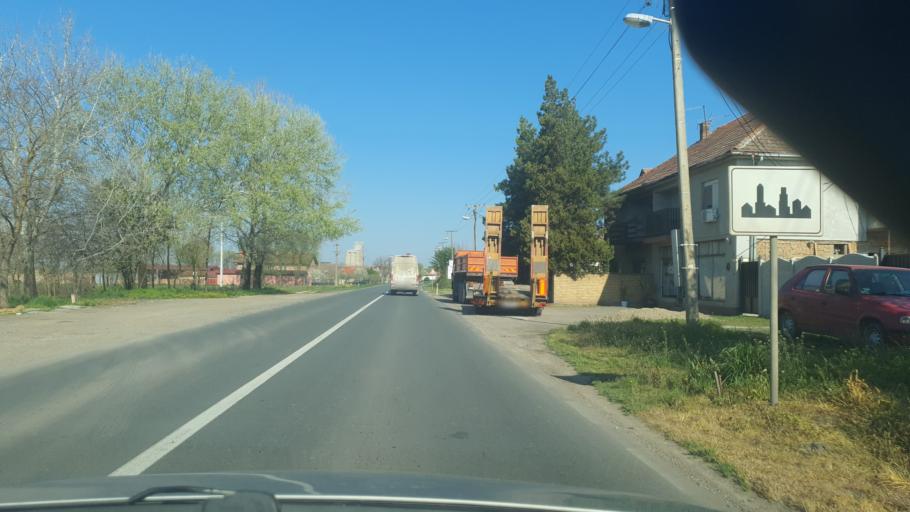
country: RS
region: Autonomna Pokrajina Vojvodina
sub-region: Zapadnobacki Okrug
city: Kula
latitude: 45.6861
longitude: 19.3940
